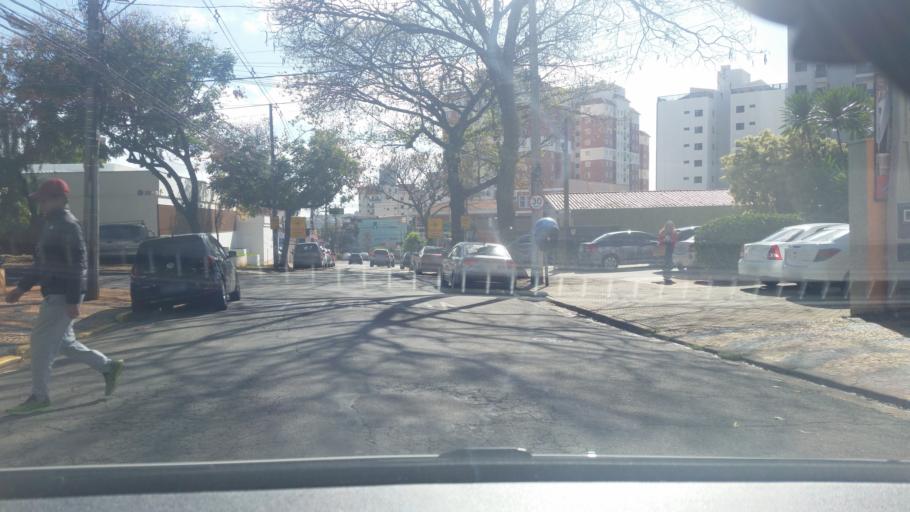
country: BR
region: Sao Paulo
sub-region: Campinas
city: Campinas
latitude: -22.8840
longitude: -47.0689
